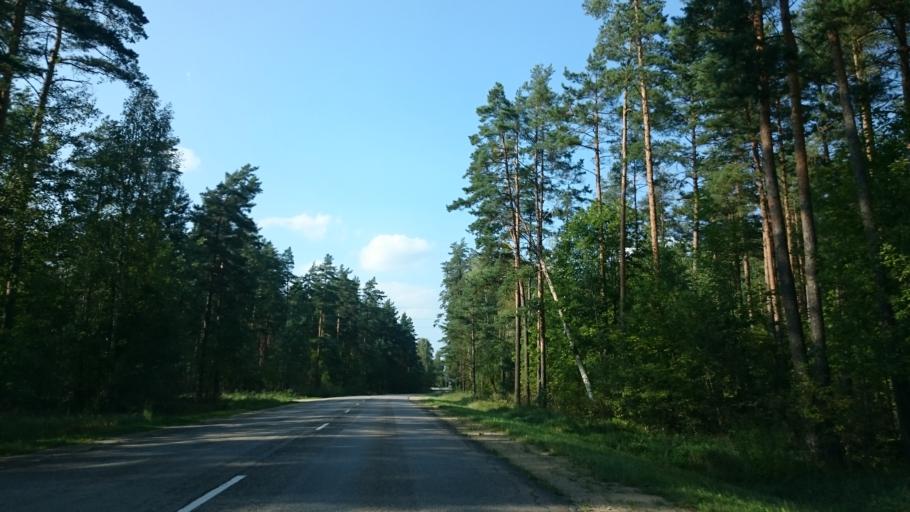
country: LV
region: Stopini
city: Ulbroka
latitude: 56.9583
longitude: 24.3070
